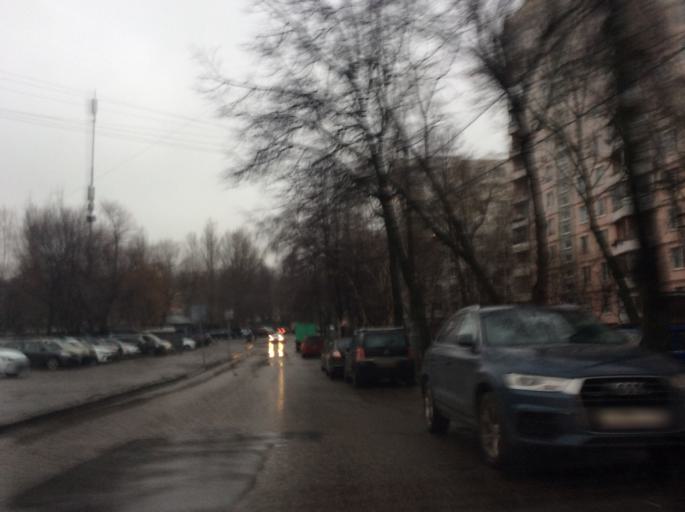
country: RU
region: Moscow
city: Tyoply Stan
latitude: 55.6390
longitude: 37.5178
